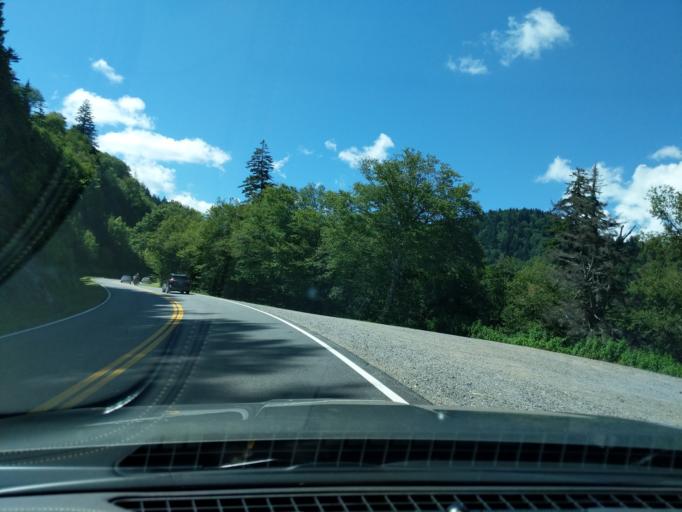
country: US
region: Tennessee
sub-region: Sevier County
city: Gatlinburg
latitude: 35.6036
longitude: -83.4284
